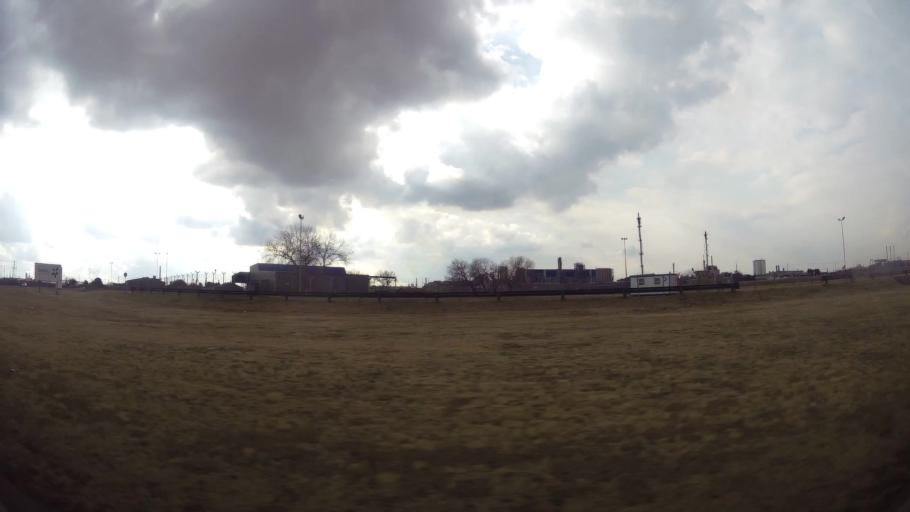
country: ZA
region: Orange Free State
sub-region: Fezile Dabi District Municipality
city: Sasolburg
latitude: -26.8365
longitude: 27.8705
